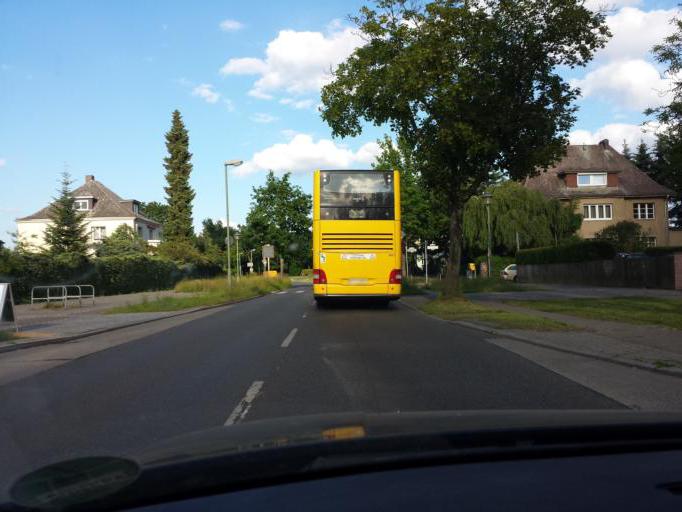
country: DE
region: Berlin
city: Britz
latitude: 52.4391
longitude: 13.4094
